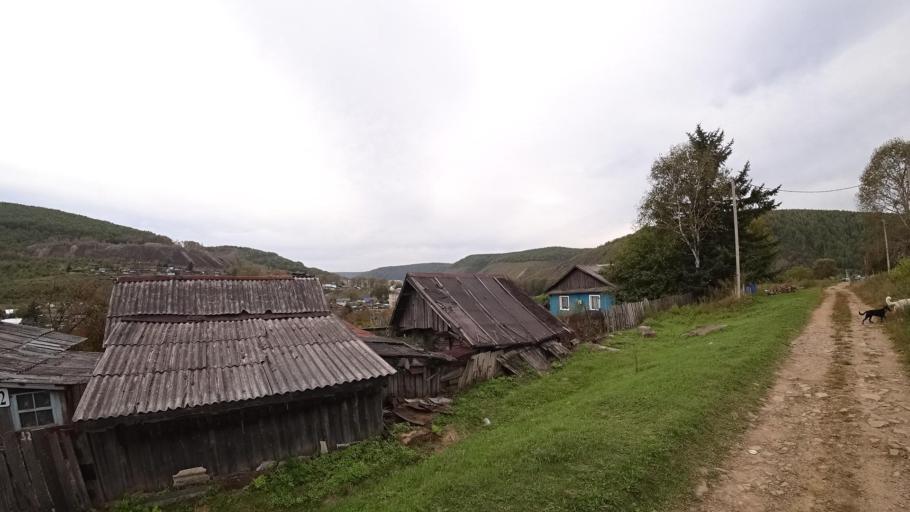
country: RU
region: Jewish Autonomous Oblast
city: Khingansk
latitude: 49.1274
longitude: 131.2038
